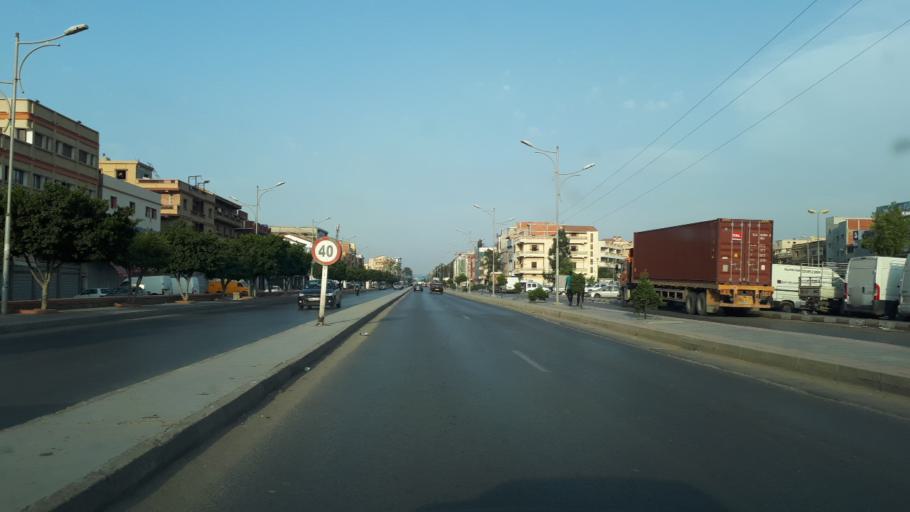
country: DZ
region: Alger
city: Dar el Beida
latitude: 36.7300
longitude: 3.2321
